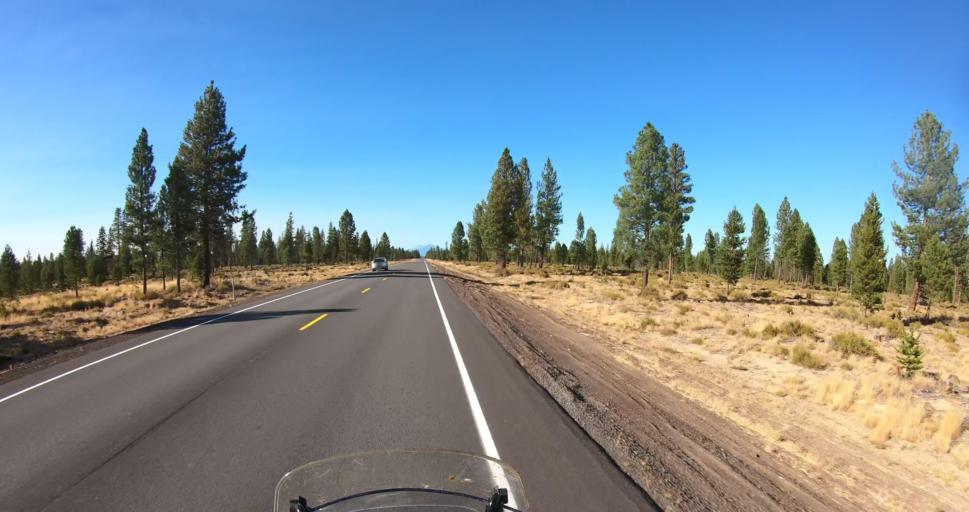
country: US
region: Oregon
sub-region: Deschutes County
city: La Pine
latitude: 43.5450
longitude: -121.4685
